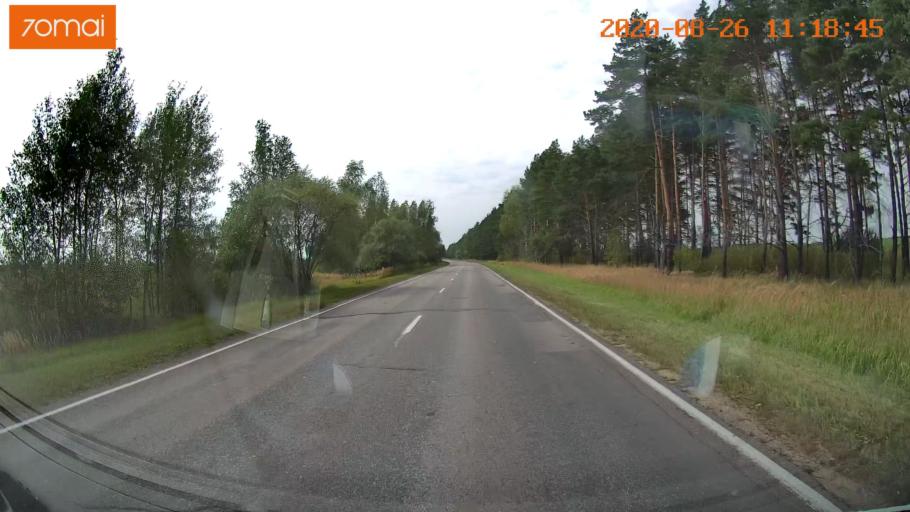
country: RU
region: Rjazan
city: Shilovo
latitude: 54.4069
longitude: 41.0916
